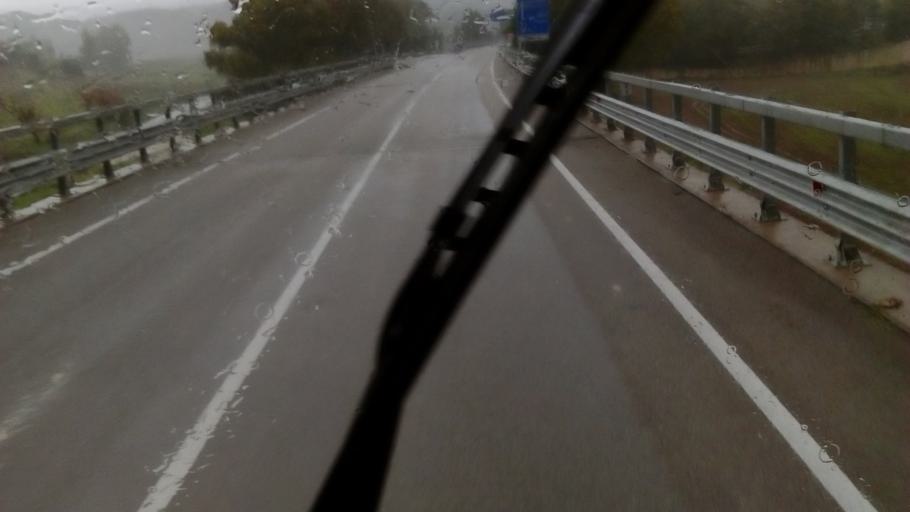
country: IT
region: Sicily
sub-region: Enna
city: Pietraperzia
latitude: 37.4947
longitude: 14.1471
